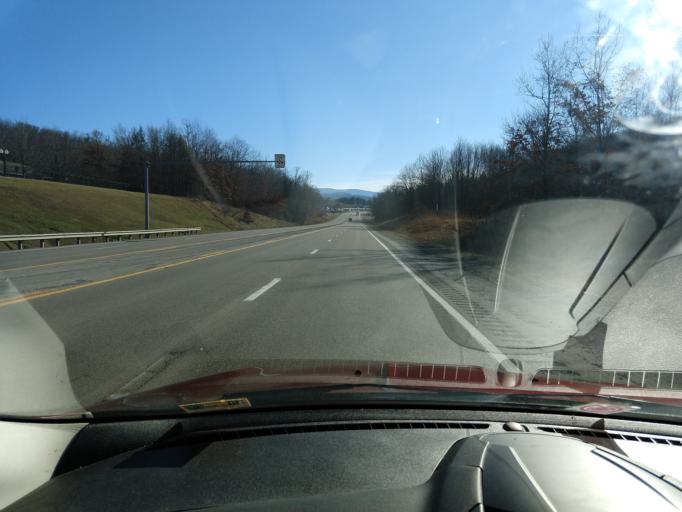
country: US
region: West Virginia
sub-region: Randolph County
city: Elkins
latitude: 38.8817
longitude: -79.8434
